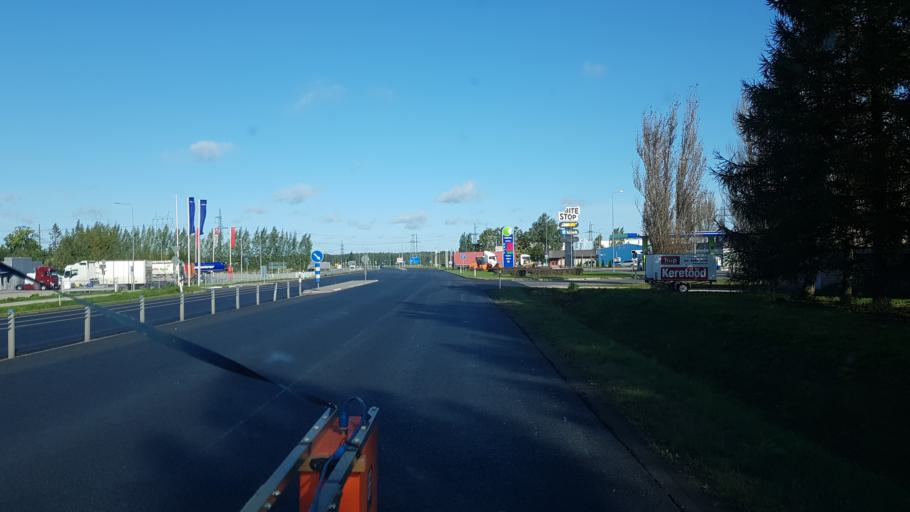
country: EE
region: Tartu
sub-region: Tartu linn
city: Tartu
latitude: 58.3753
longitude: 26.6823
